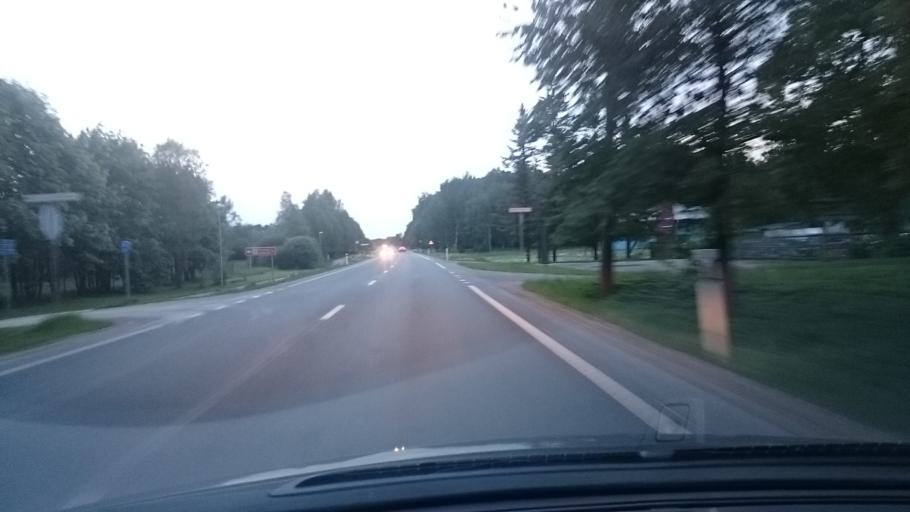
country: EE
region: Raplamaa
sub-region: Kehtna vald
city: Kehtna
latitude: 58.9787
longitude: 24.8466
